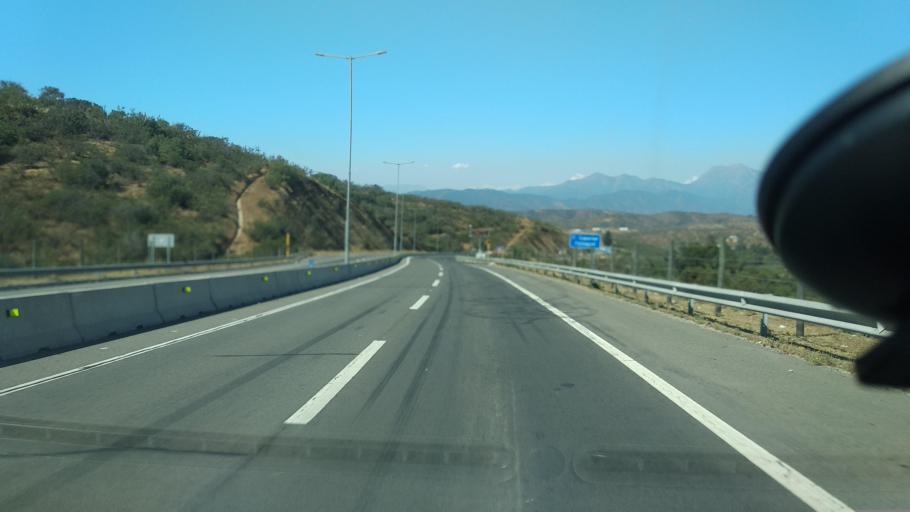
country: CL
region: Valparaiso
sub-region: Provincia de Marga Marga
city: Villa Alemana
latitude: -33.0470
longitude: -71.3256
